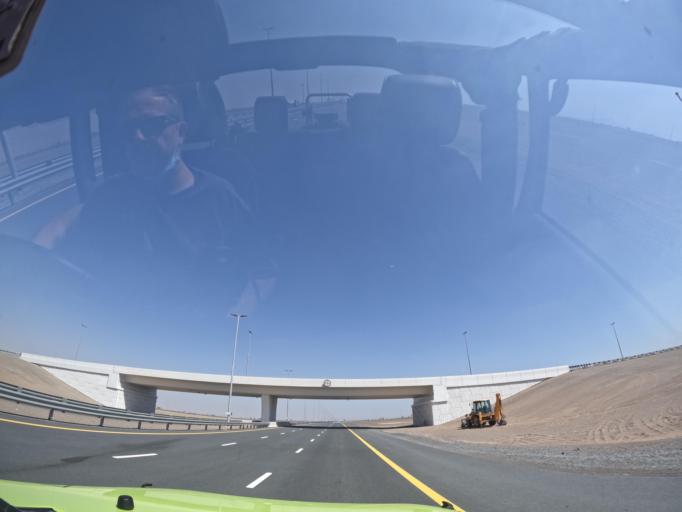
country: AE
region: Ash Shariqah
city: Adh Dhayd
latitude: 25.0467
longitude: 55.8932
